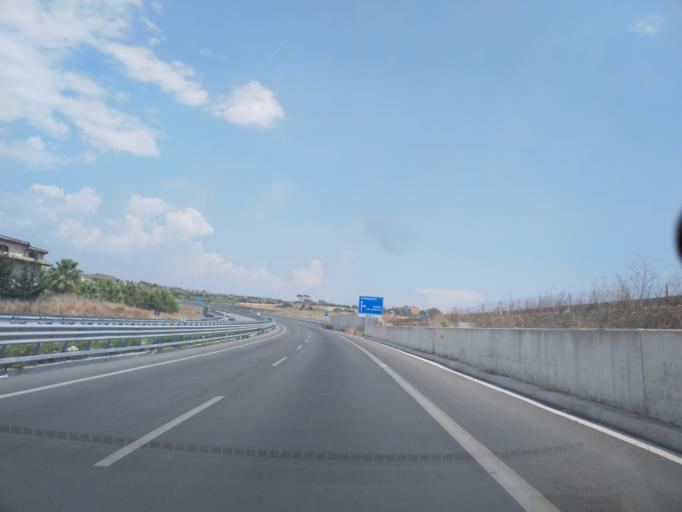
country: IT
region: Sicily
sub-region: Agrigento
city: Favara
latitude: 37.3490
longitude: 13.6692
